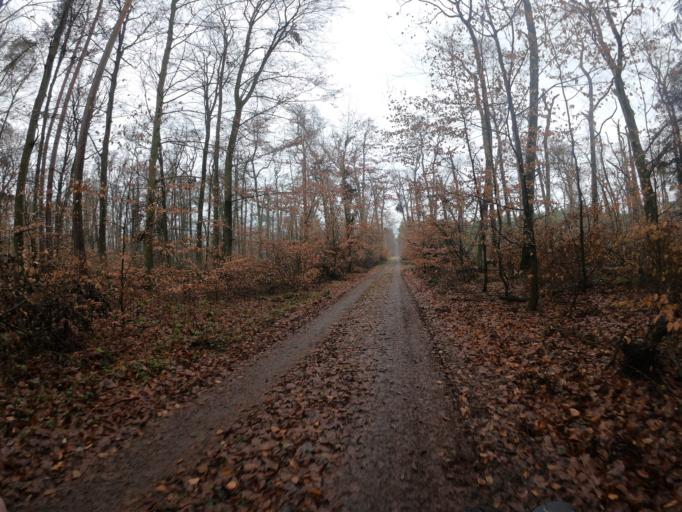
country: DE
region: Hesse
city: Morfelden-Walldorf
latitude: 49.9767
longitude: 8.6095
